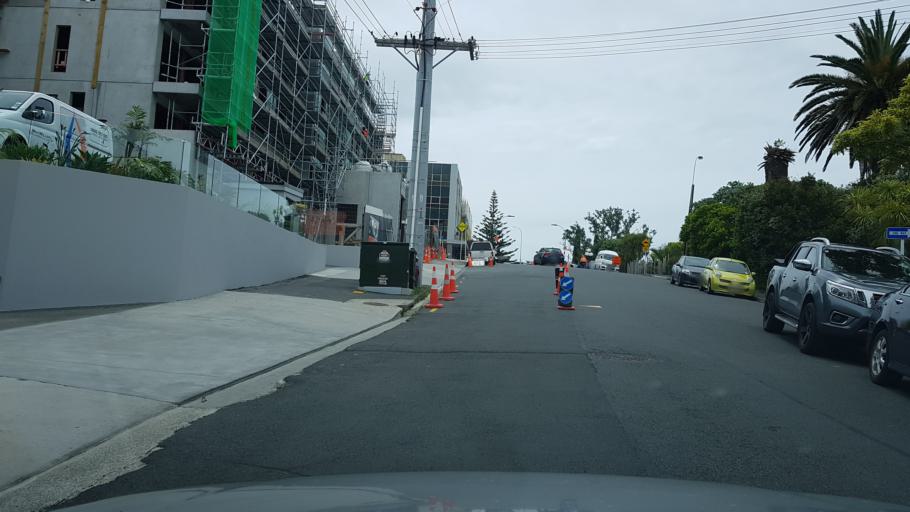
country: NZ
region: Auckland
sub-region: Auckland
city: North Shore
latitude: -36.8137
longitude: 174.7258
